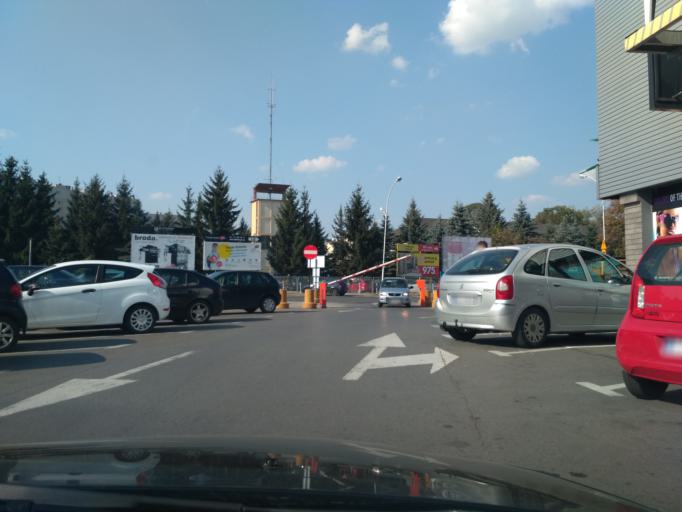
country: PL
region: Subcarpathian Voivodeship
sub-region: Rzeszow
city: Rzeszow
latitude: 50.0355
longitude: 21.9958
